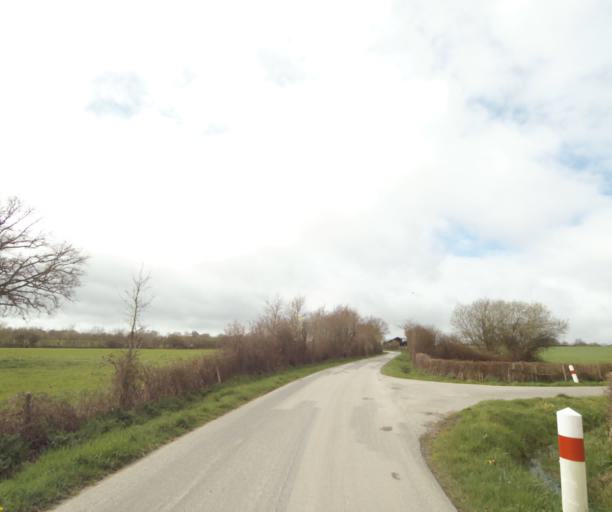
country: FR
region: Pays de la Loire
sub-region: Departement de la Loire-Atlantique
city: Bouvron
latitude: 47.4320
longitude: -1.8953
